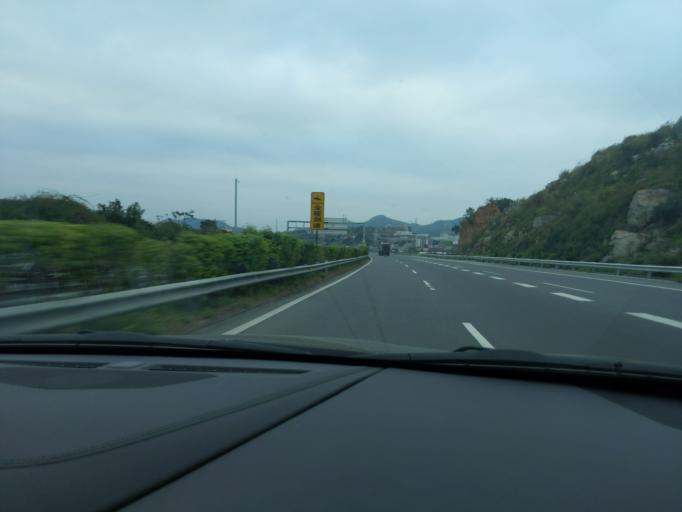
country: CN
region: Fujian
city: Neikeng
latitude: 24.7846
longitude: 118.4834
